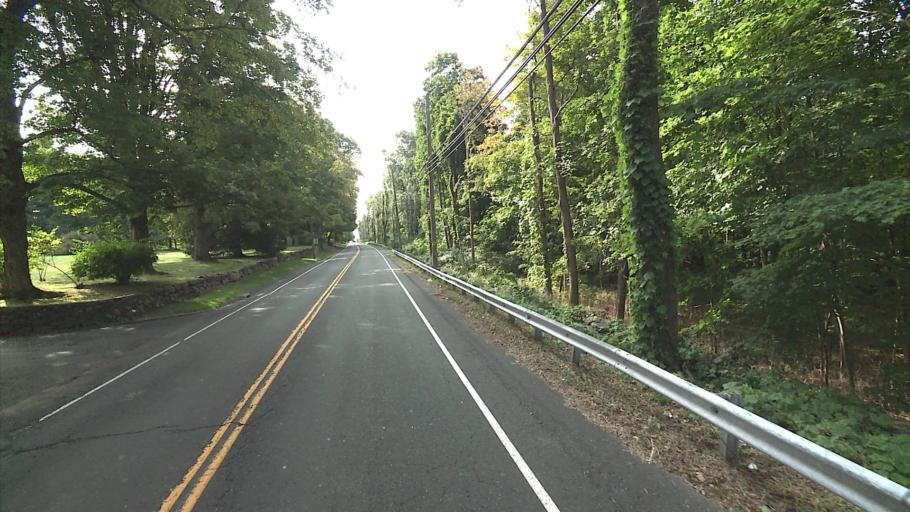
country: US
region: Connecticut
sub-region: Fairfield County
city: New Canaan
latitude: 41.1778
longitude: -73.4986
